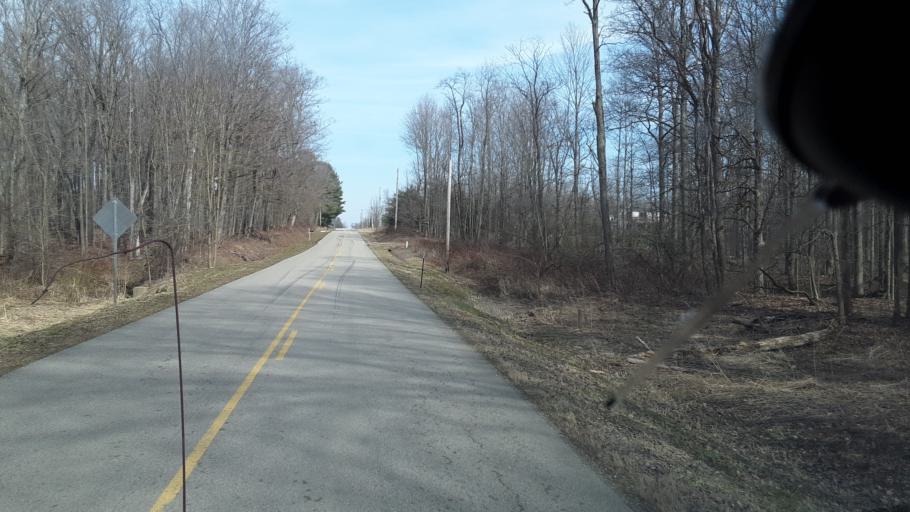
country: US
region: Ohio
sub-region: Ashtabula County
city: Jefferson
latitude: 41.7641
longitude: -80.7904
